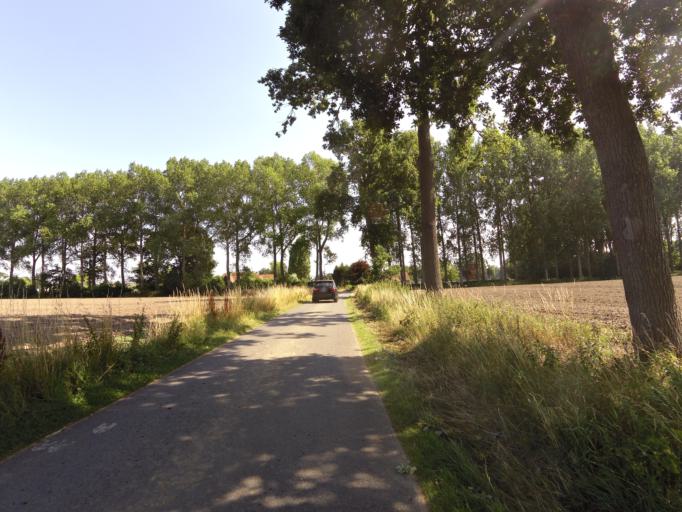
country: BE
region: Flanders
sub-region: Provincie West-Vlaanderen
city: Jabbeke
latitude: 51.2014
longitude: 3.1385
